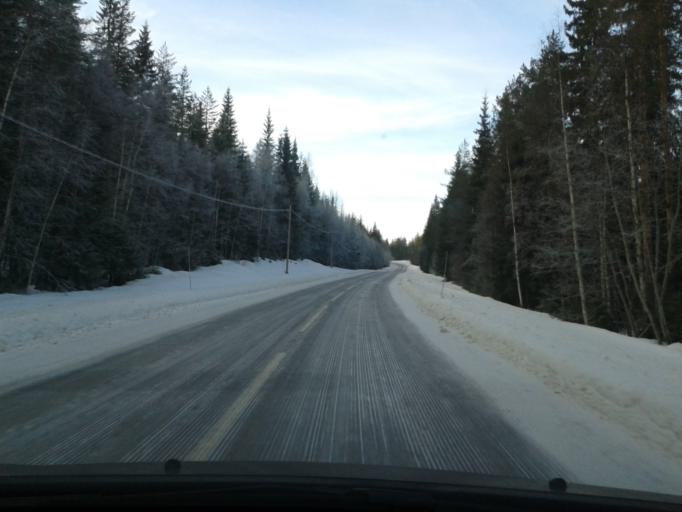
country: SE
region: Vaesternorrland
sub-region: OErnskoeldsviks Kommun
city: Bredbyn
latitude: 63.6593
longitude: 17.8573
